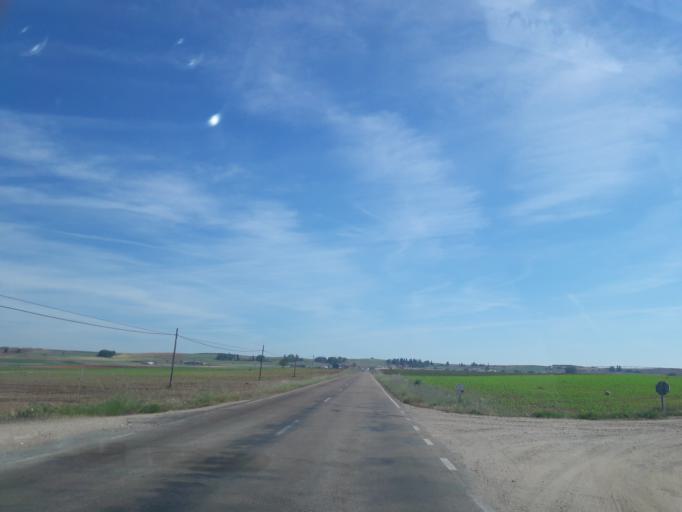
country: ES
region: Castille and Leon
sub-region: Provincia de Salamanca
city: Villoruela
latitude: 40.9906
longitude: -5.4048
